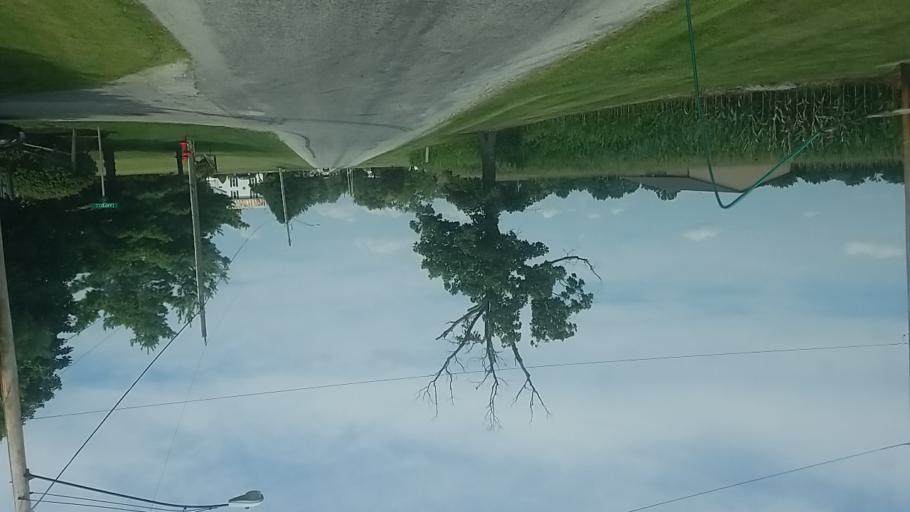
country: US
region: Ohio
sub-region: Hardin County
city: Forest
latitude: 40.8036
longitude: -83.5228
